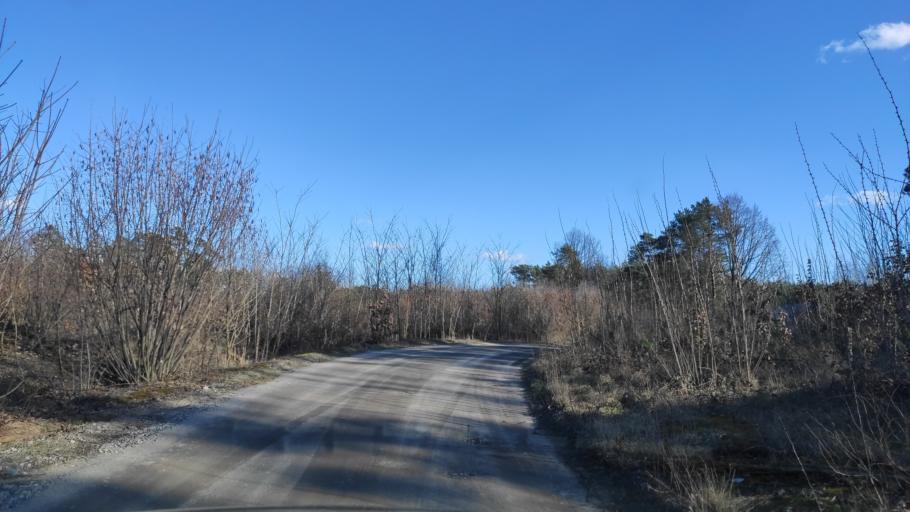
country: PL
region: Masovian Voivodeship
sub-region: Powiat radomski
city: Jastrzebia
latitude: 51.4554
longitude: 21.2737
